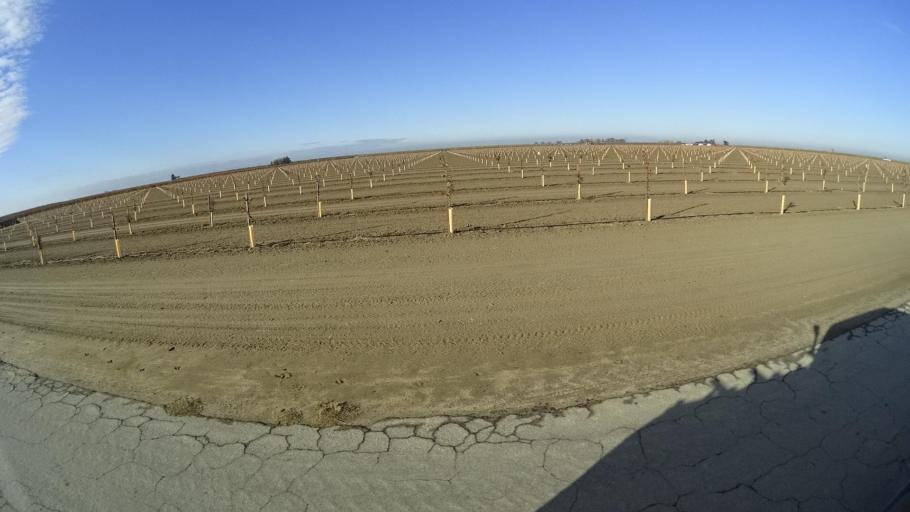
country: US
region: California
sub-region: Kern County
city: Delano
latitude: 35.7120
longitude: -119.3029
